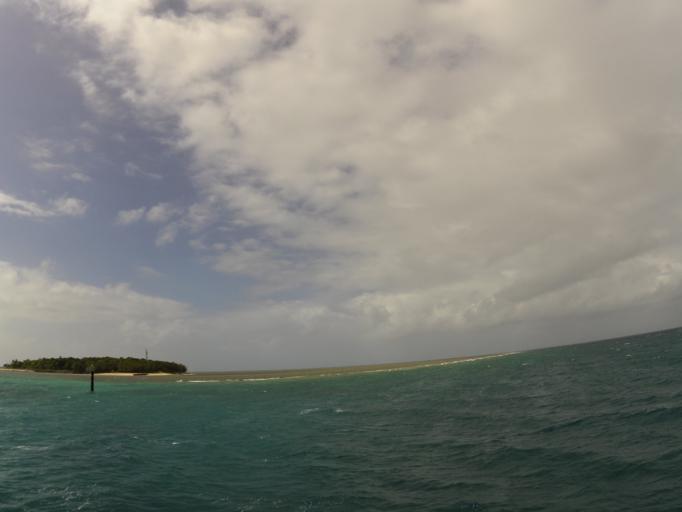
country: AU
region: Queensland
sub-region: Cairns
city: Yorkeys Knob
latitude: -16.7602
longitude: 145.9636
